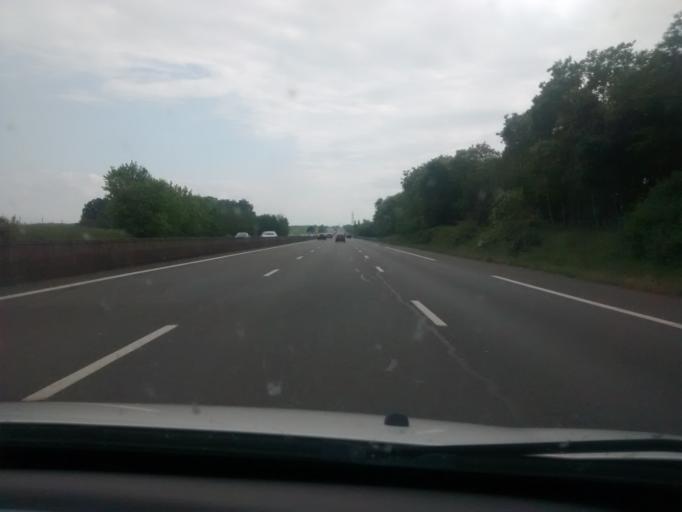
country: FR
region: Centre
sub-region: Departement d'Eure-et-Loir
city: Morancez
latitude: 48.4033
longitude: 1.4994
